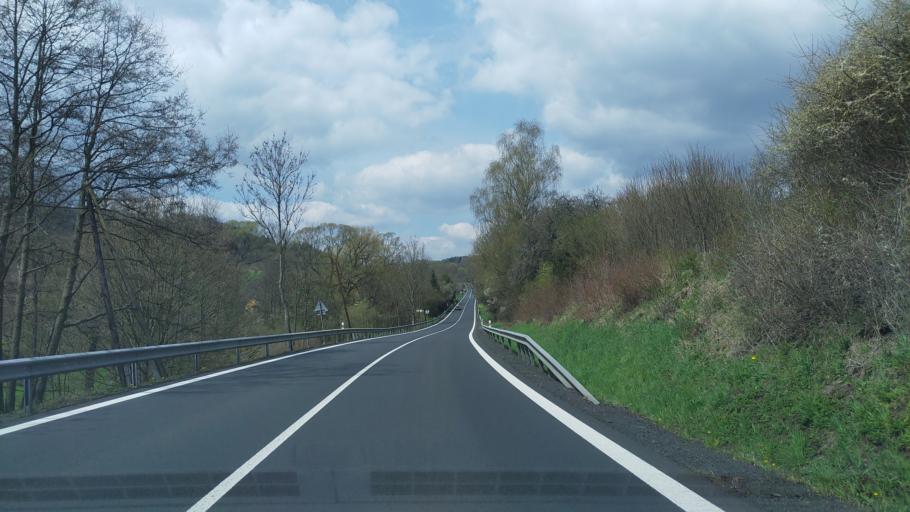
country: CZ
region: Karlovarsky
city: Ostrov
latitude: 50.3307
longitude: 13.0167
